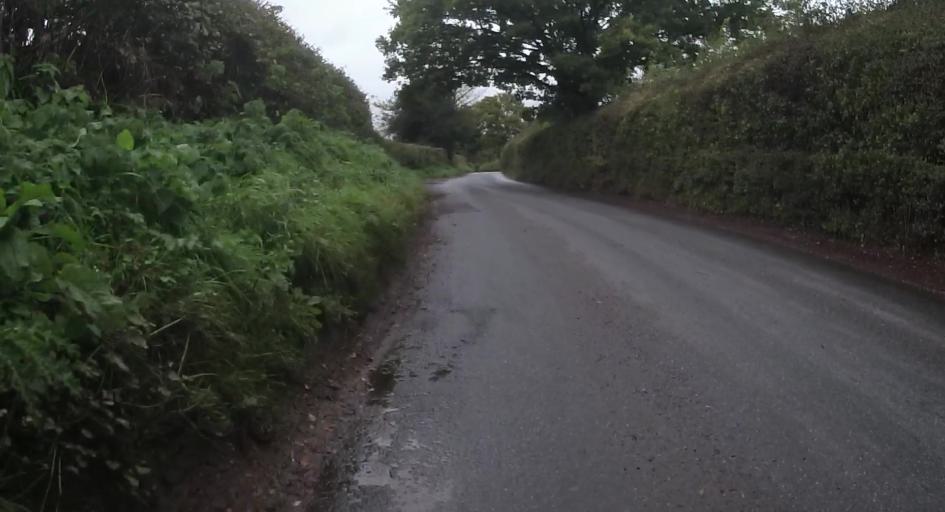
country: GB
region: England
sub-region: Hampshire
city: Tadley
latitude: 51.4106
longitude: -1.1736
